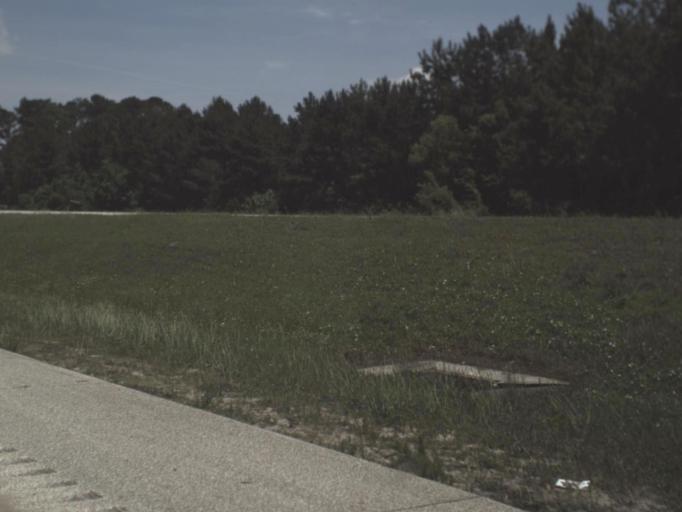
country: US
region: Florida
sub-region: Saint Johns County
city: Fruit Cove
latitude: 30.1670
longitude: -81.5668
